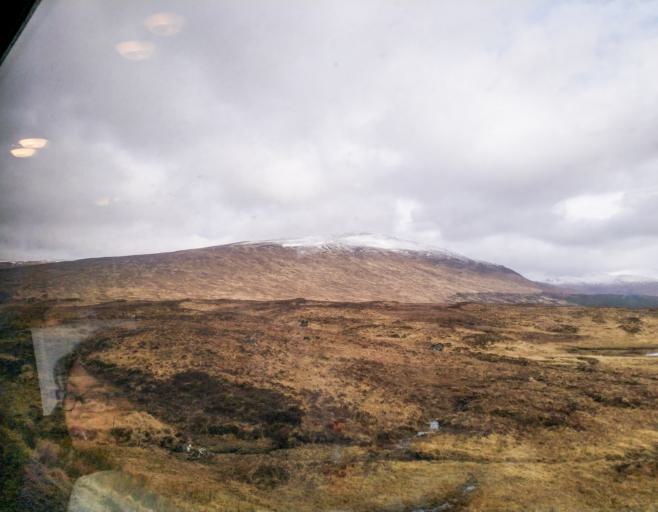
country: GB
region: Scotland
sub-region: Highland
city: Spean Bridge
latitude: 56.7565
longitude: -4.6860
